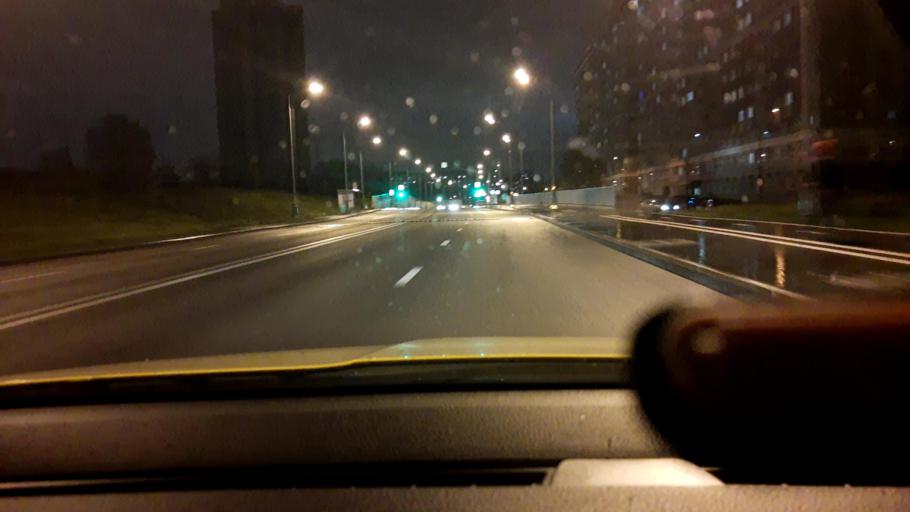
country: RU
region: Moscow
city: Ramenki
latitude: 55.6896
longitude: 37.5175
